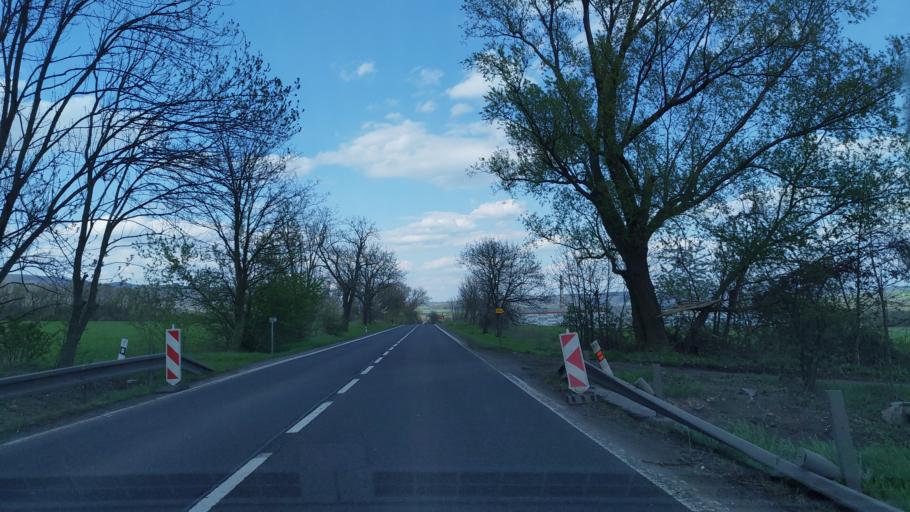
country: CZ
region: Ustecky
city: Chabarovice
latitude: 50.6794
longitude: 13.9081
